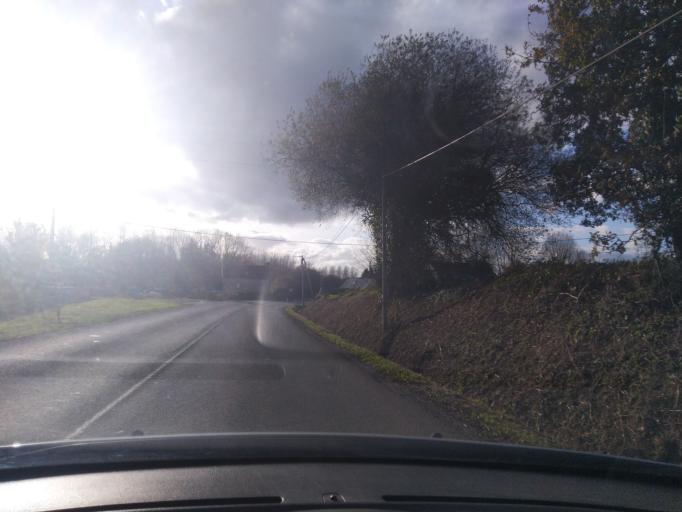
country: FR
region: Brittany
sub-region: Departement du Finistere
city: Guerlesquin
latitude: 48.5659
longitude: -3.6117
